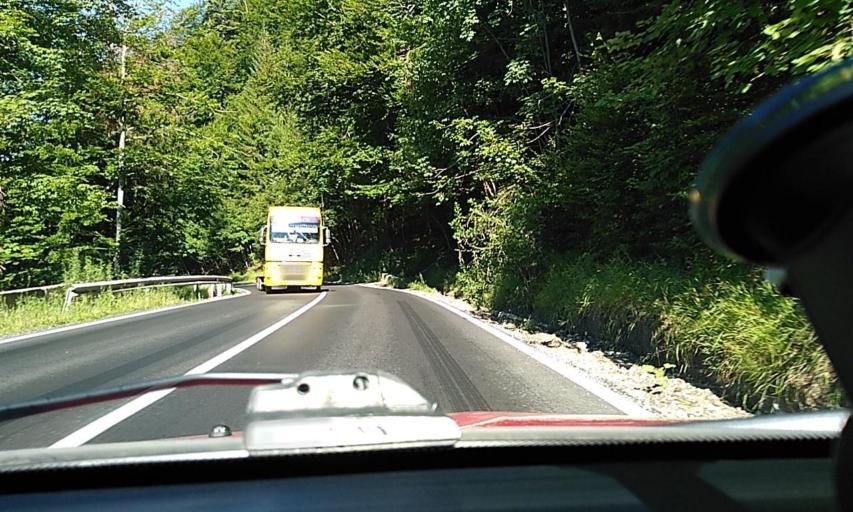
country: RO
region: Brasov
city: Crivina
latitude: 45.4890
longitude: 25.8798
